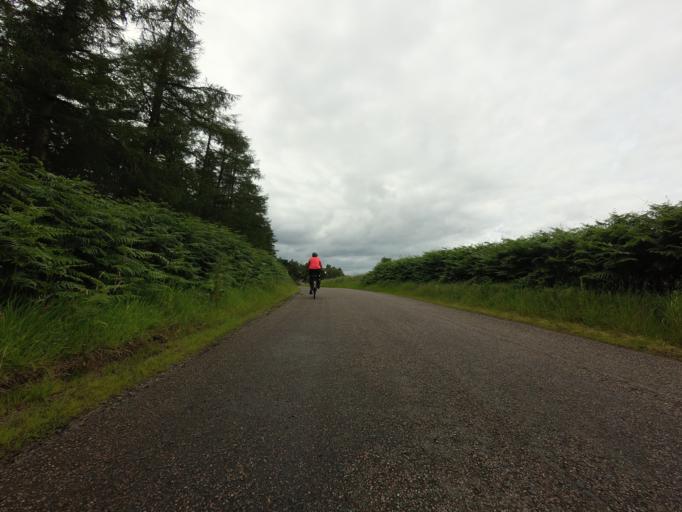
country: GB
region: Scotland
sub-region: Moray
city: Forres
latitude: 57.6037
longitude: -3.7438
